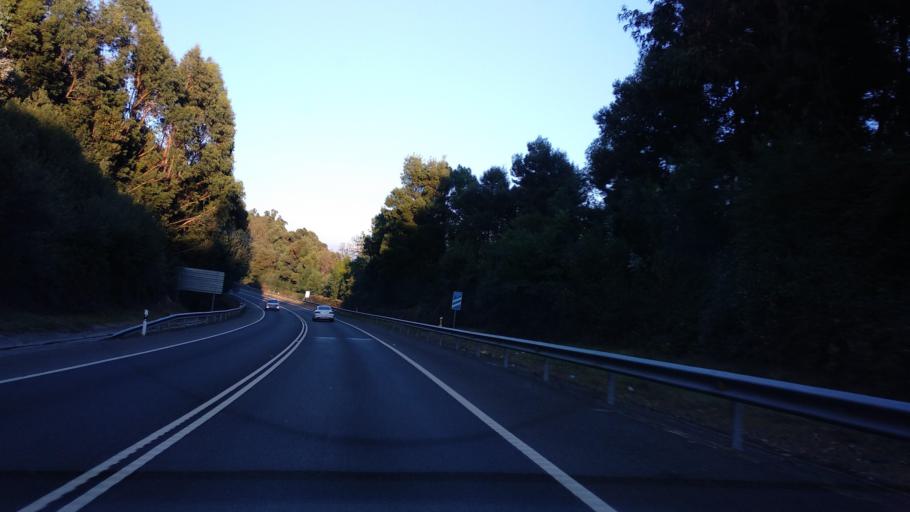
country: ES
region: Galicia
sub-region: Provincia de Pontevedra
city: Moana
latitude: 42.2820
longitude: -8.7617
